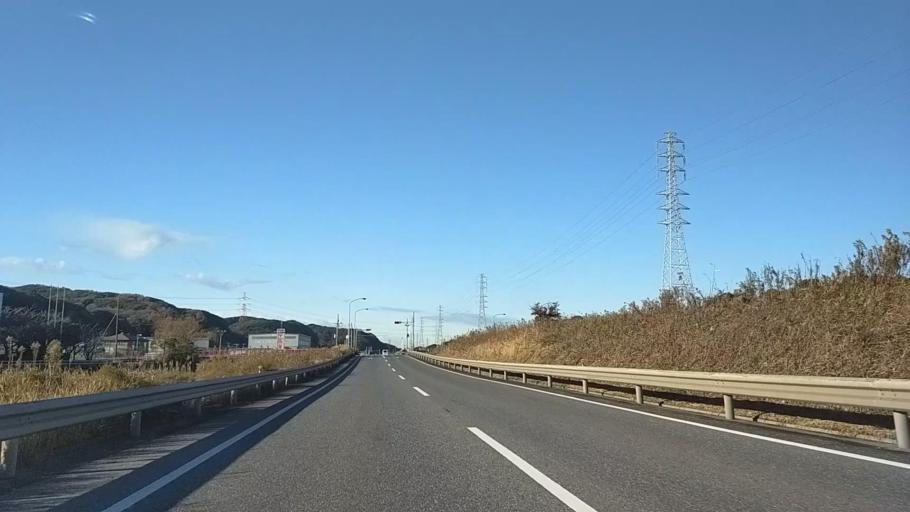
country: JP
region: Chiba
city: Kimitsu
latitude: 35.3510
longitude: 139.8984
